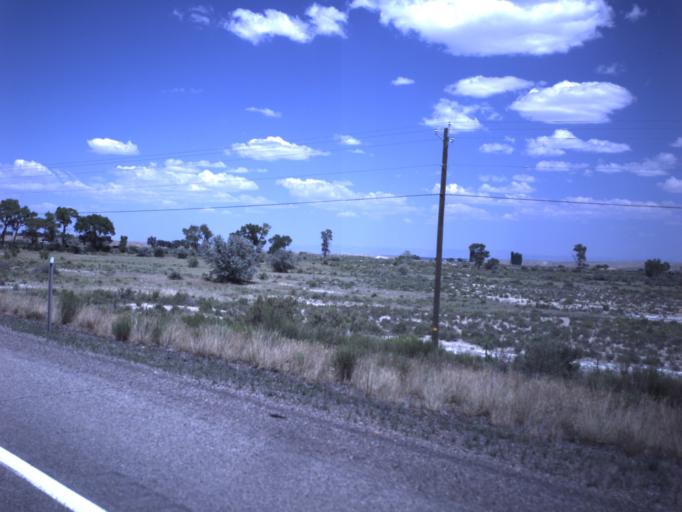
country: US
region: Utah
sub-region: Emery County
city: Castle Dale
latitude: 39.1921
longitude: -111.0243
